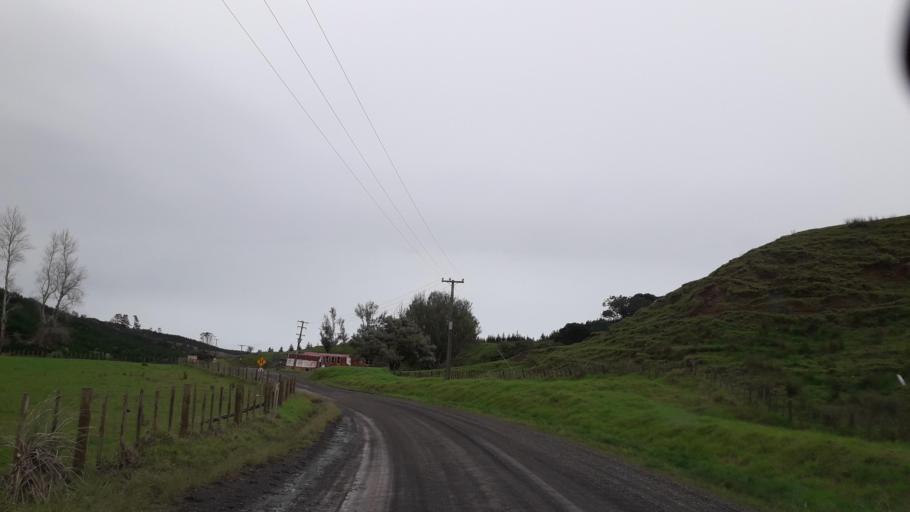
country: NZ
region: Northland
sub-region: Far North District
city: Ahipara
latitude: -35.4239
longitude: 173.3582
